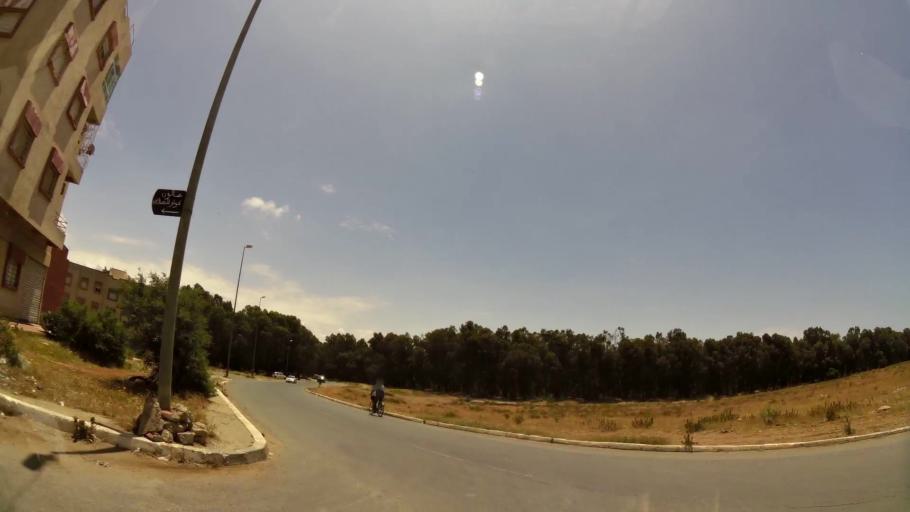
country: MA
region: Gharb-Chrarda-Beni Hssen
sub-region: Kenitra Province
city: Kenitra
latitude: 34.2481
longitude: -6.6227
